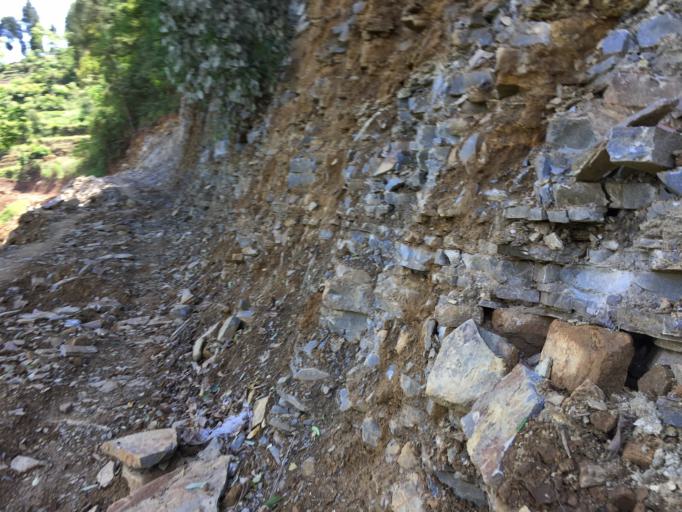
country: CN
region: Guizhou Sheng
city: Shiqian
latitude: 27.6748
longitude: 108.0837
